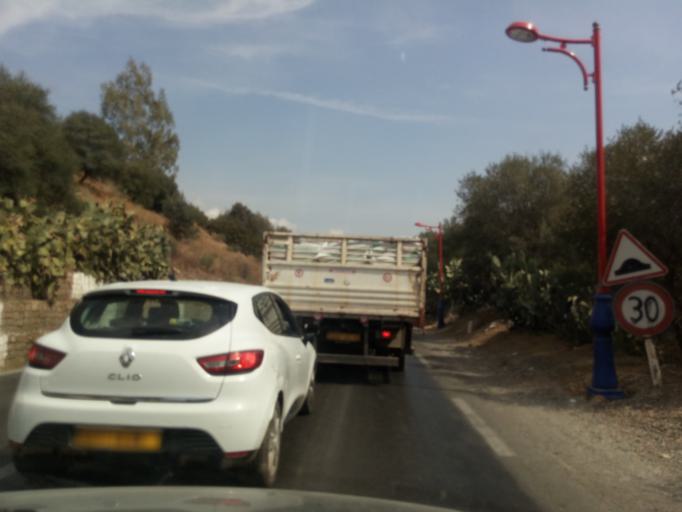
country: DZ
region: Tizi Ouzou
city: Chemini
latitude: 36.5777
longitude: 4.6482
